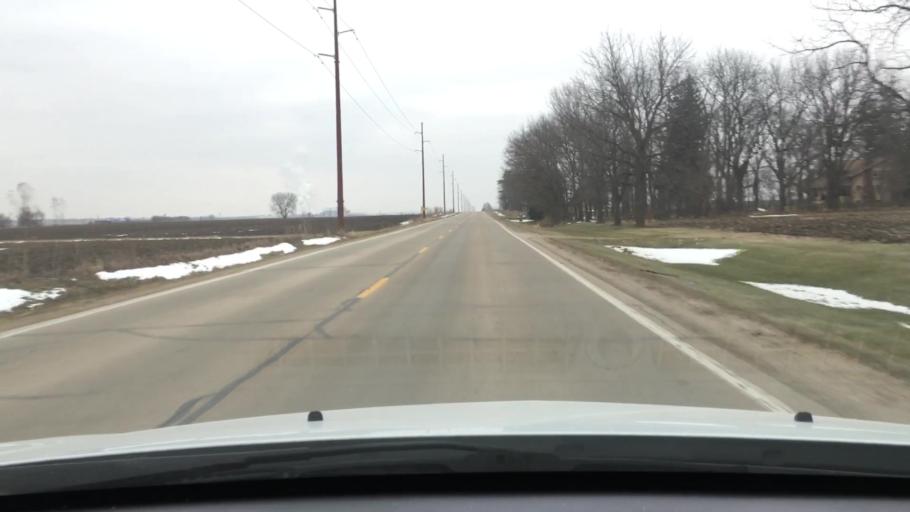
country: US
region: Illinois
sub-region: Ogle County
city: Rochelle
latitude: 41.8554
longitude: -89.0247
